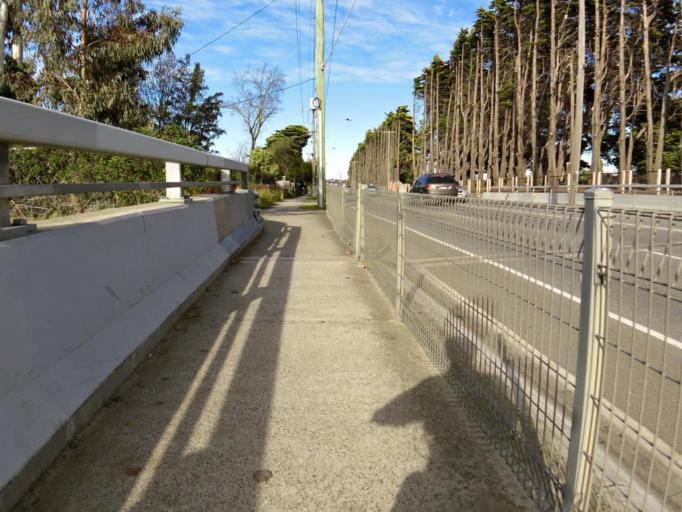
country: AU
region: Victoria
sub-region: Whitehorse
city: Box Hill
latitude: -37.8216
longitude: 145.1381
